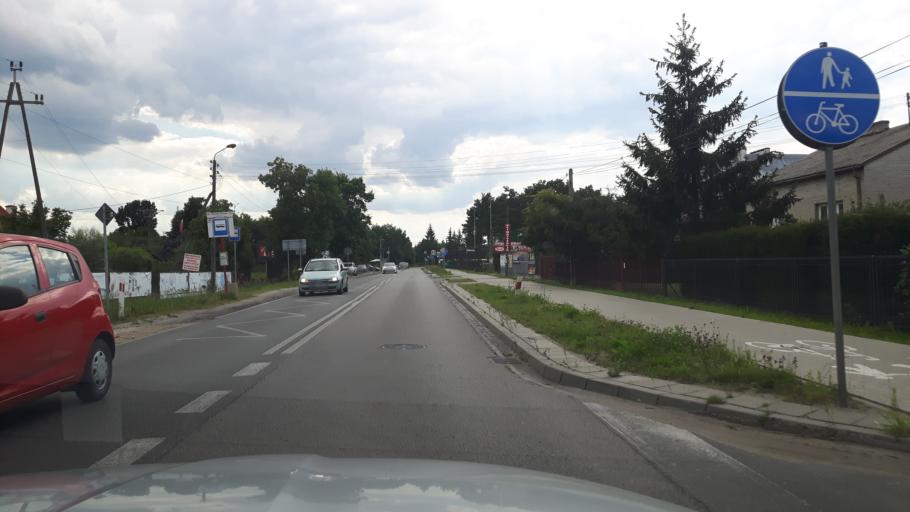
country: PL
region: Masovian Voivodeship
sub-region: Powiat wolominski
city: Duczki
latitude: 52.3628
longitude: 21.2918
